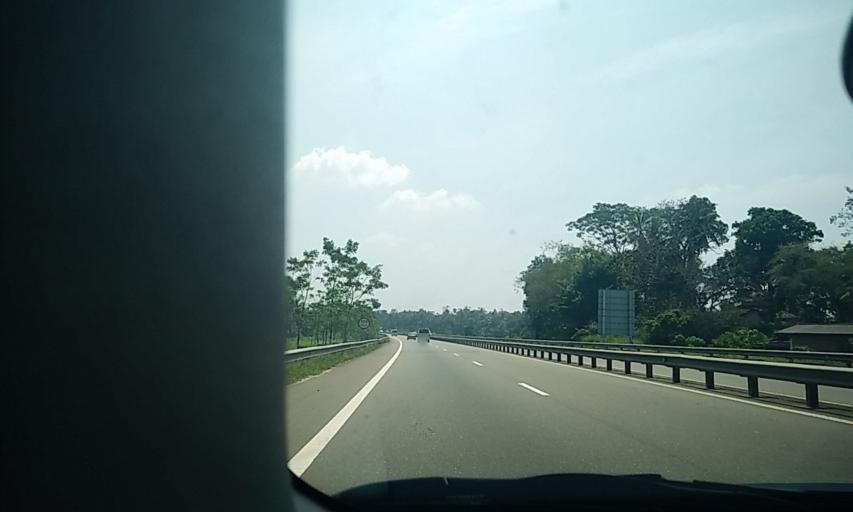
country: LK
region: Western
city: Homagama
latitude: 6.7733
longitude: 79.9813
